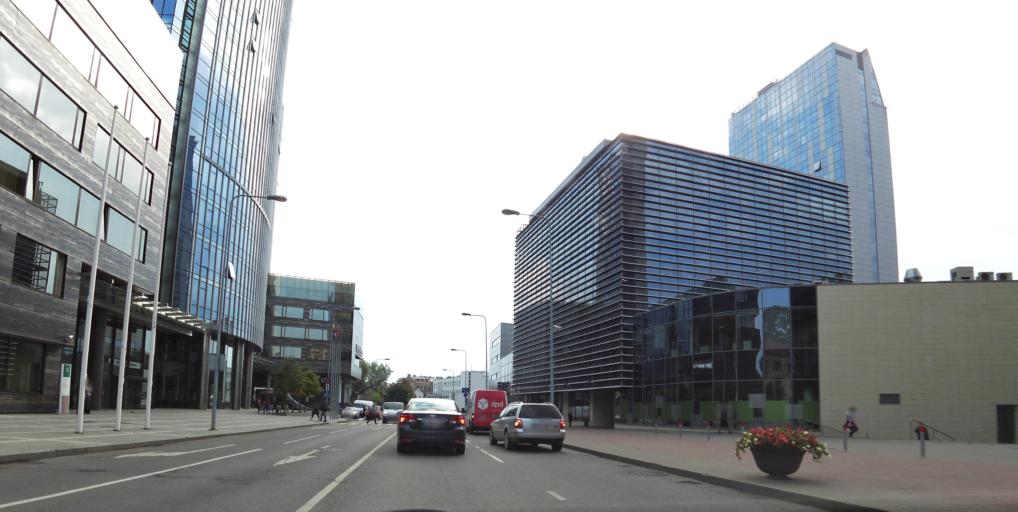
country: LT
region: Vilnius County
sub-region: Vilnius
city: Vilnius
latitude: 54.6967
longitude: 25.2781
